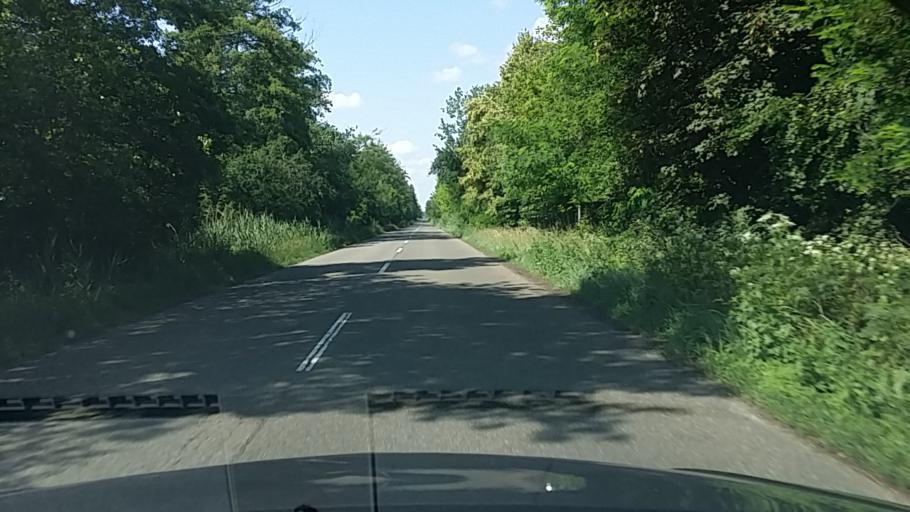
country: HU
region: Komarom-Esztergom
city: Esztergom
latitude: 47.8973
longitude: 18.7754
